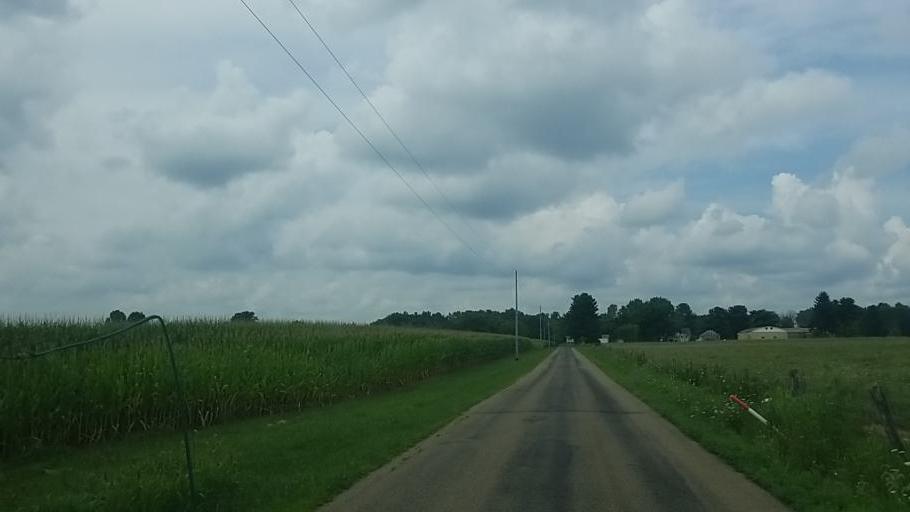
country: US
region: Ohio
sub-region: Knox County
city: Gambier
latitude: 40.3369
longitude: -82.4311
